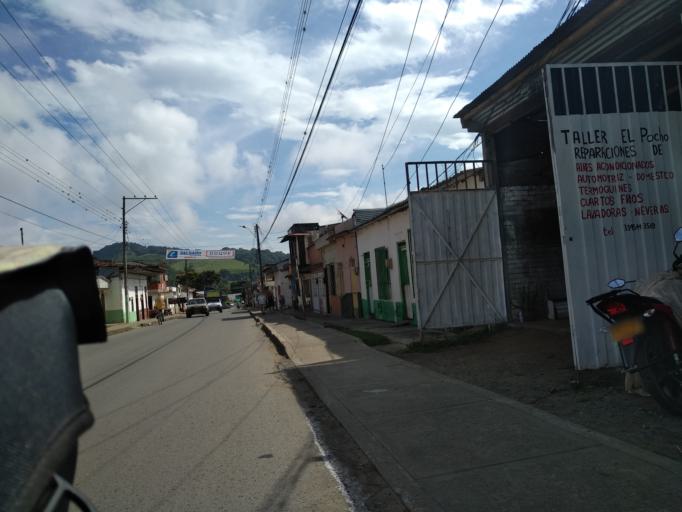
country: CO
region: Valle del Cauca
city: Caicedonia
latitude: 4.3373
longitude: -75.8289
